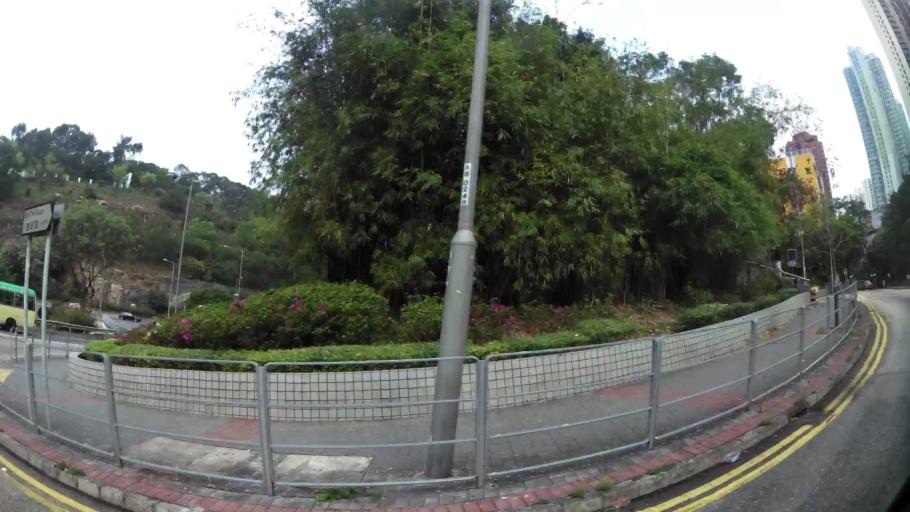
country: HK
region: Kowloon City
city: Kowloon
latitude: 22.3048
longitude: 114.2356
